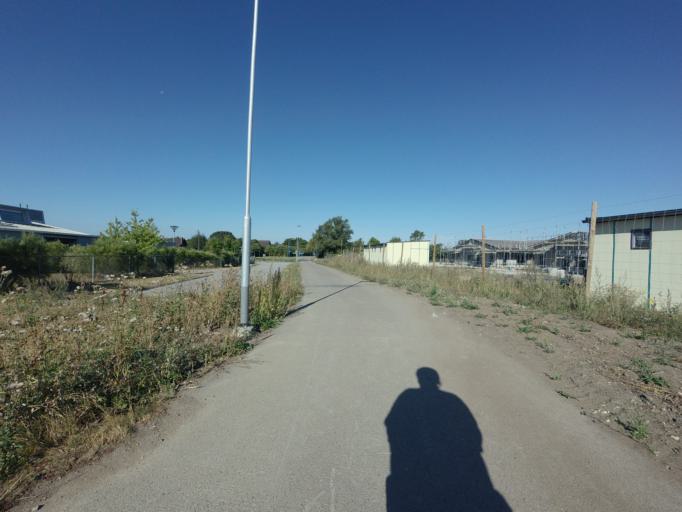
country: SE
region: Skane
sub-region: Trelleborgs Kommun
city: Skare
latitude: 55.4055
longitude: 13.0871
